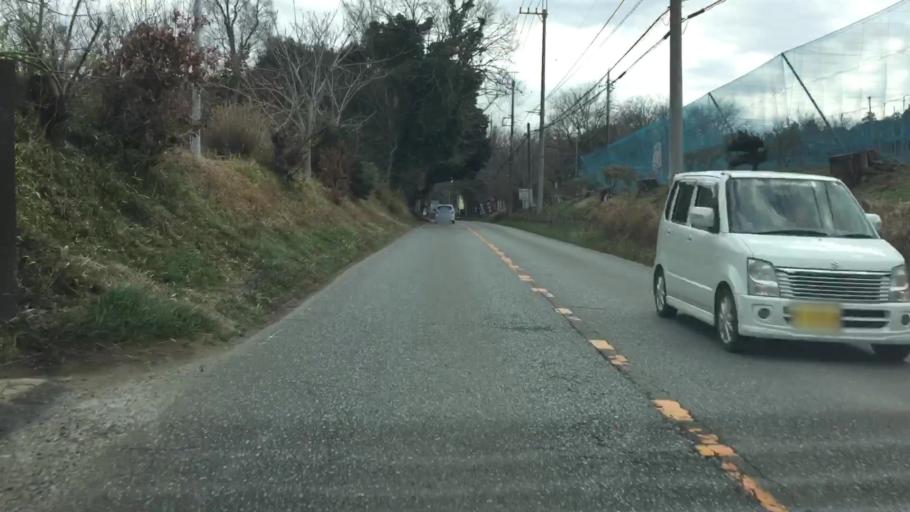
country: JP
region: Ibaraki
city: Ryugasaki
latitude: 35.8213
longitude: 140.1718
